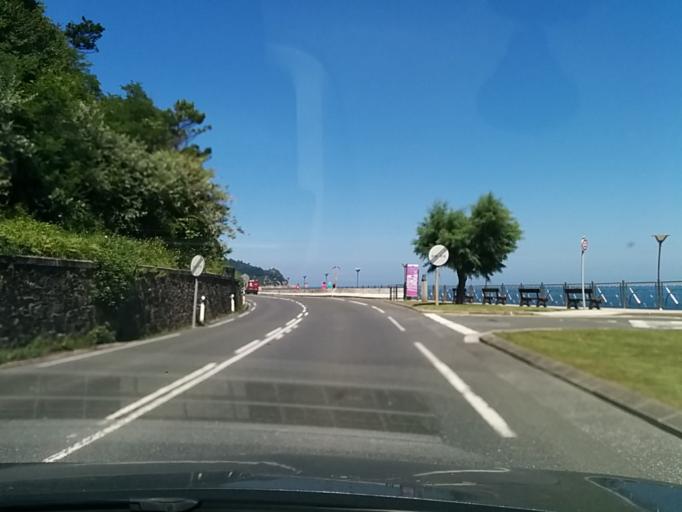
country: ES
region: Basque Country
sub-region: Provincia de Guipuzcoa
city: Zarautz
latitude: 43.2923
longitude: -2.1815
